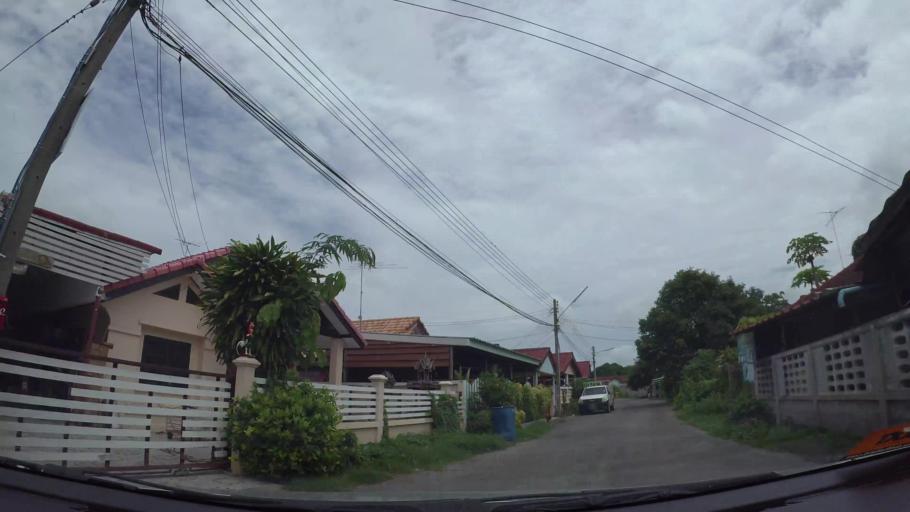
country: TH
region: Chon Buri
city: Sattahip
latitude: 12.6845
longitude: 100.9012
